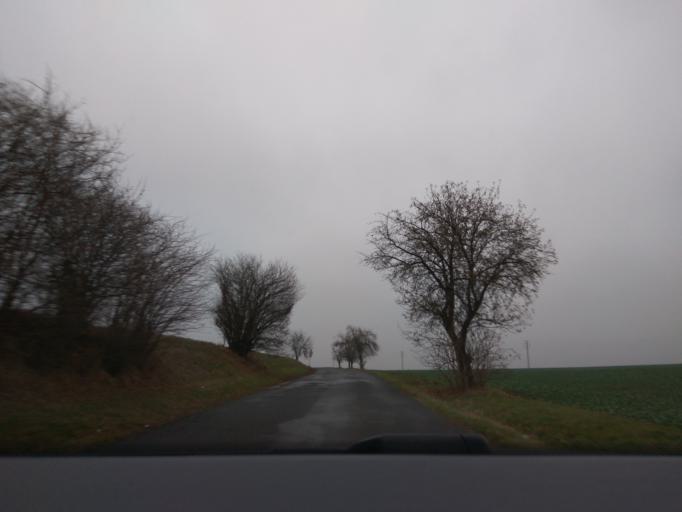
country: CZ
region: Praha
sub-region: Praha 19
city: Kbely
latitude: 50.1681
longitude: 14.5602
